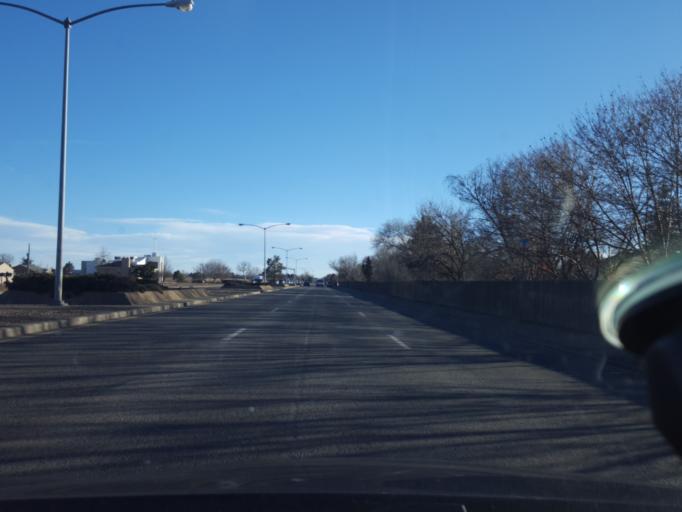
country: US
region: Colorado
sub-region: Adams County
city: Aurora
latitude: 39.7360
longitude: -104.7913
